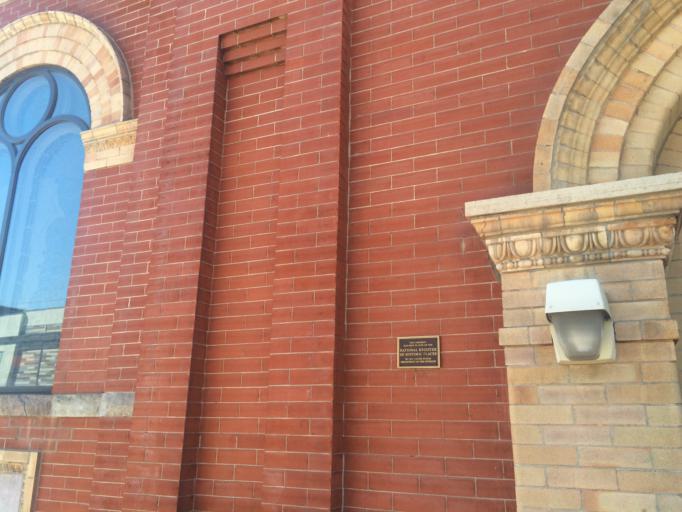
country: US
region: Colorado
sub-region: Denver County
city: Denver
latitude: 39.7666
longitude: -105.0042
